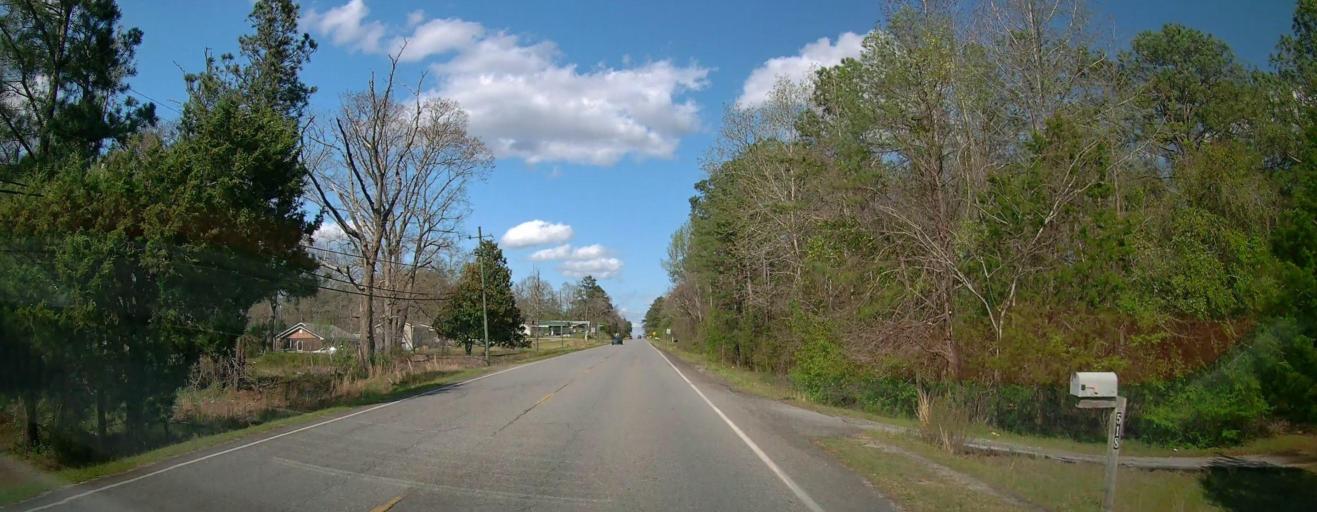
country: US
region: Georgia
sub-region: Baldwin County
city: Hardwick
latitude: 32.9798
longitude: -83.2766
